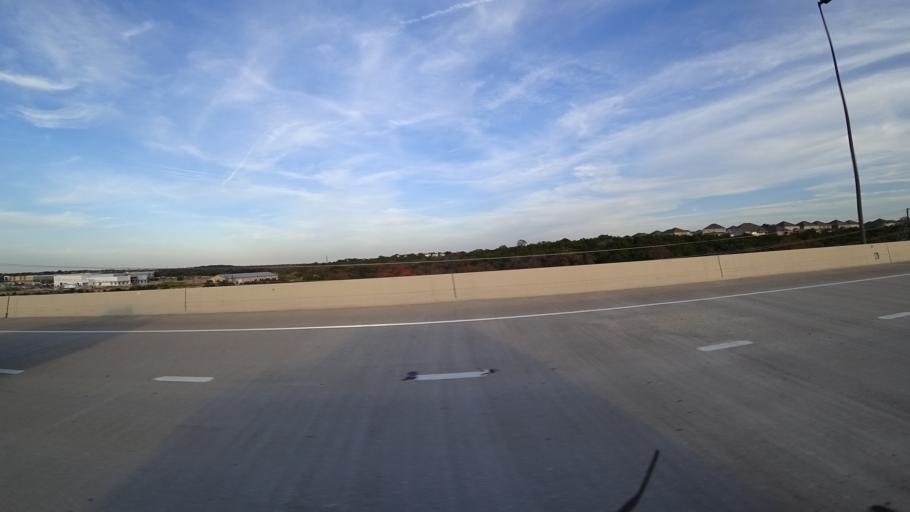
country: US
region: Texas
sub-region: Williamson County
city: Cedar Park
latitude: 30.4963
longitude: -97.8027
